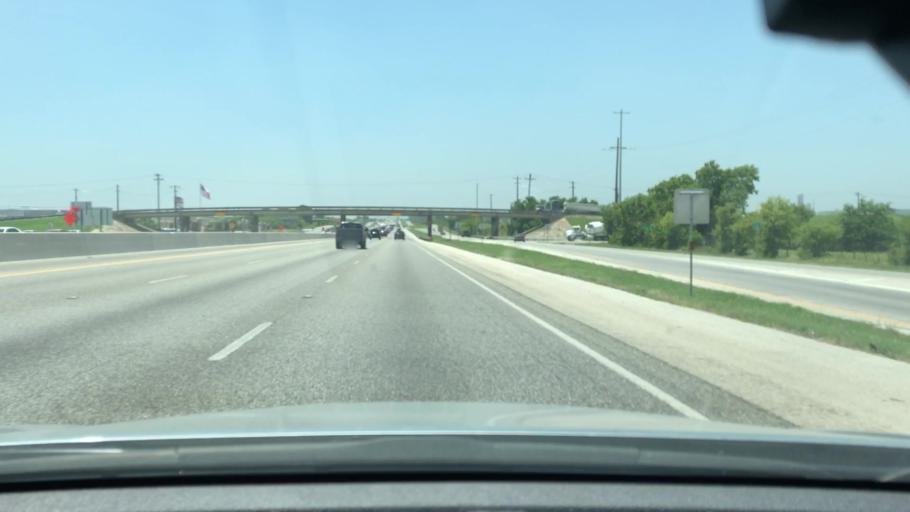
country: US
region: Texas
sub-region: Hays County
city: San Marcos
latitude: 29.8185
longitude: -97.9964
